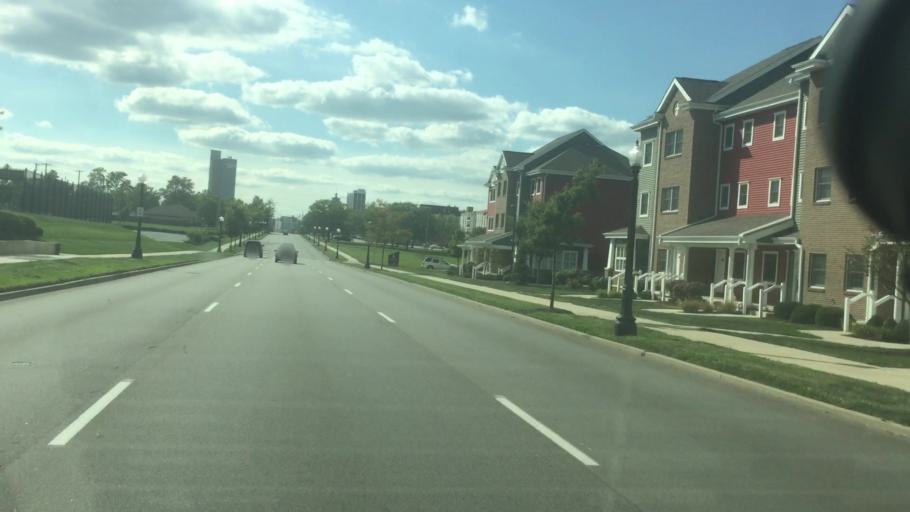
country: US
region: Indiana
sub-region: Allen County
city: Fort Wayne
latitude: 41.0790
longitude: -85.1209
